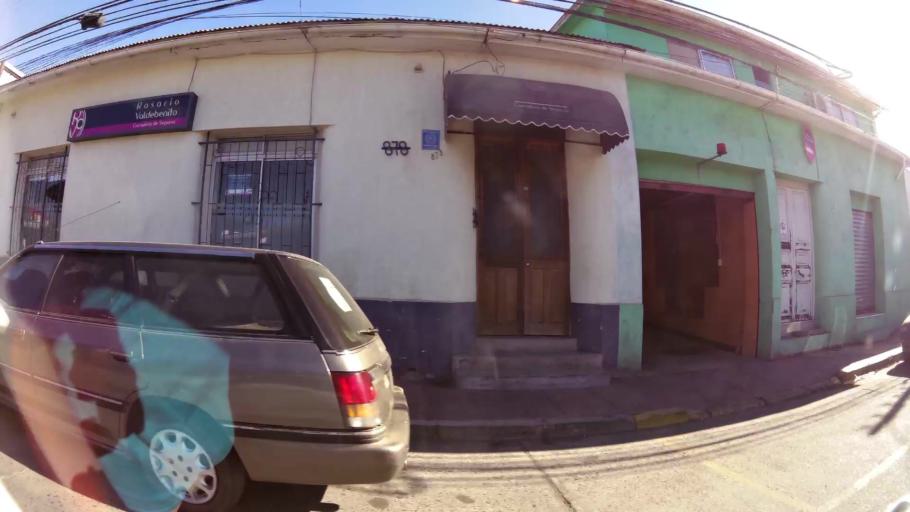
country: CL
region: O'Higgins
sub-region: Provincia de Colchagua
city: Chimbarongo
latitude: -34.5916
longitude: -70.9870
